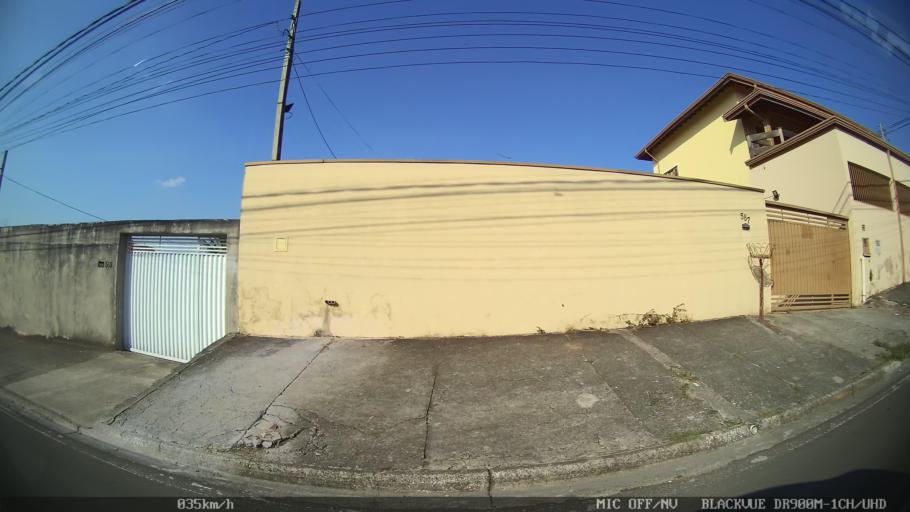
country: BR
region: Sao Paulo
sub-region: Campinas
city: Campinas
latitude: -22.9851
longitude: -47.1411
